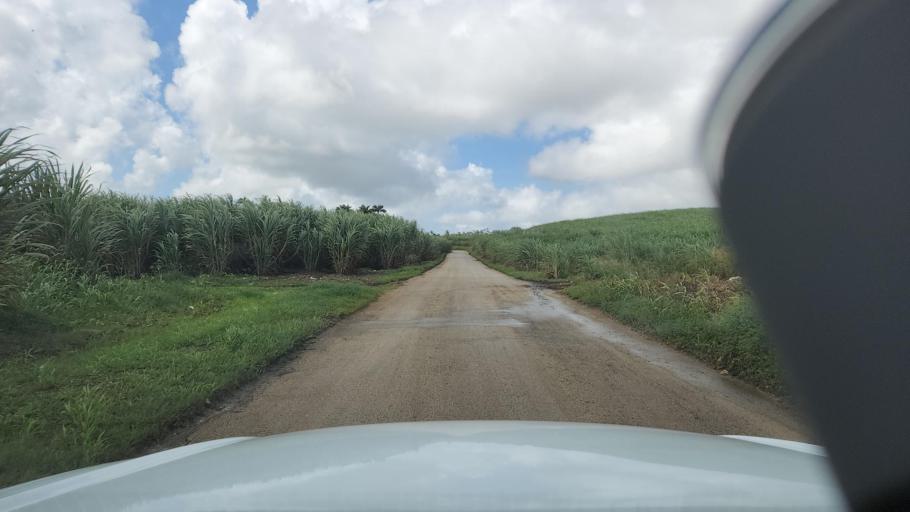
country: BB
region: Saint Joseph
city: Bathsheba
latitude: 13.1952
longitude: -59.5217
